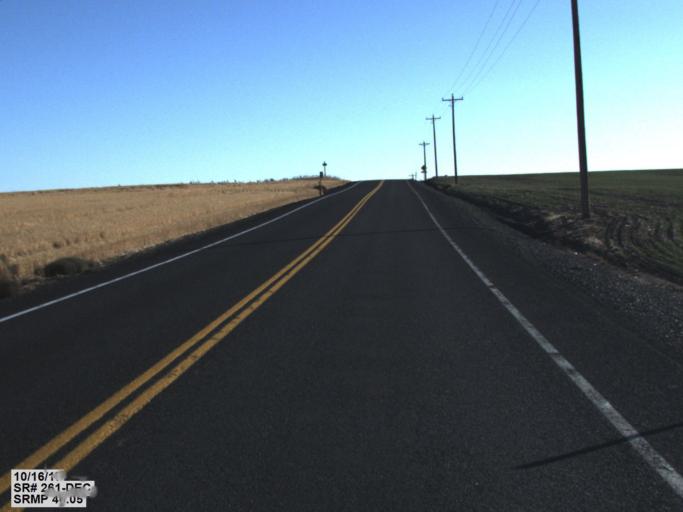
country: US
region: Washington
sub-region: Adams County
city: Ritzville
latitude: 46.8864
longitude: -118.3344
